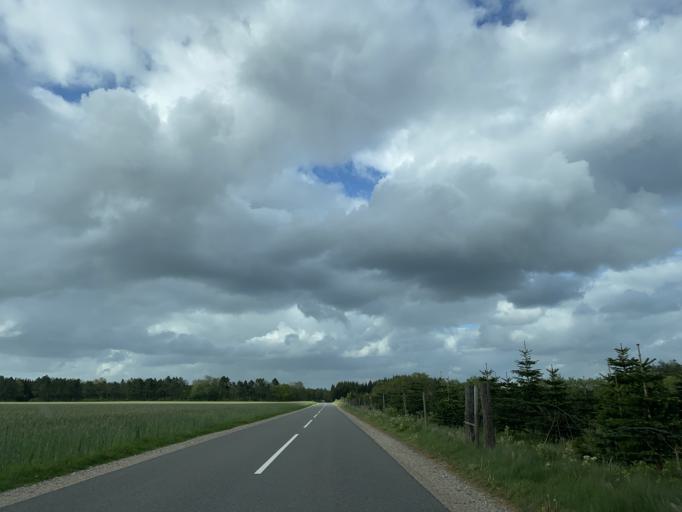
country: DK
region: Central Jutland
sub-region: Horsens Kommune
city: Braedstrup
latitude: 56.0383
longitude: 9.6626
